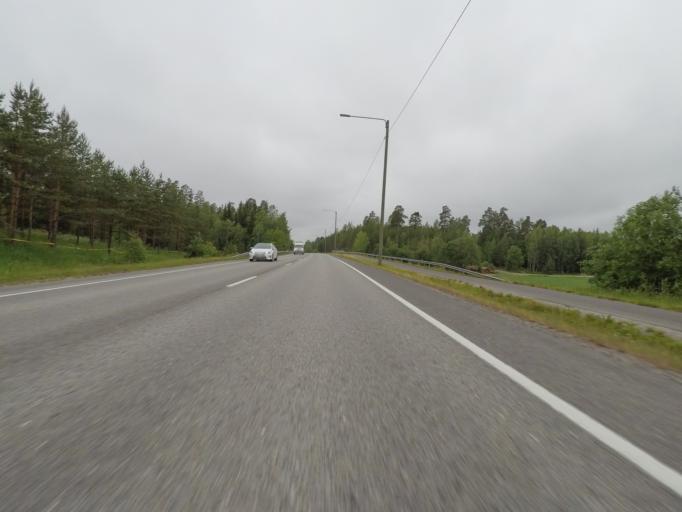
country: FI
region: Varsinais-Suomi
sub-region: Turku
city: Naantali
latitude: 60.4687
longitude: 22.0891
